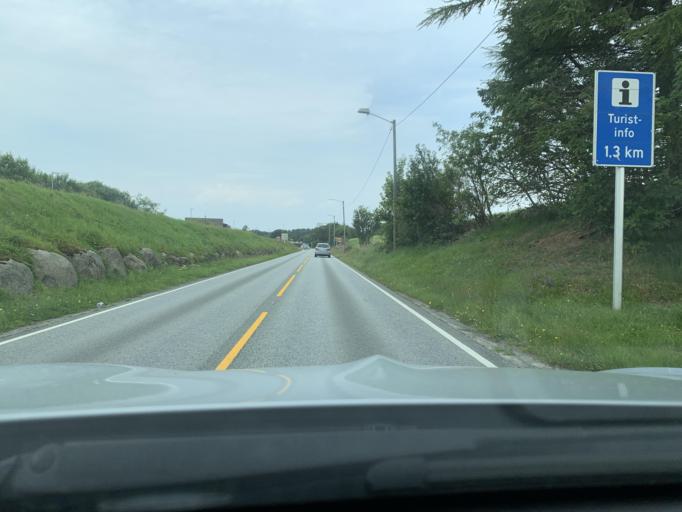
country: NO
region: Rogaland
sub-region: Time
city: Bryne
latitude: 58.7341
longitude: 5.6740
